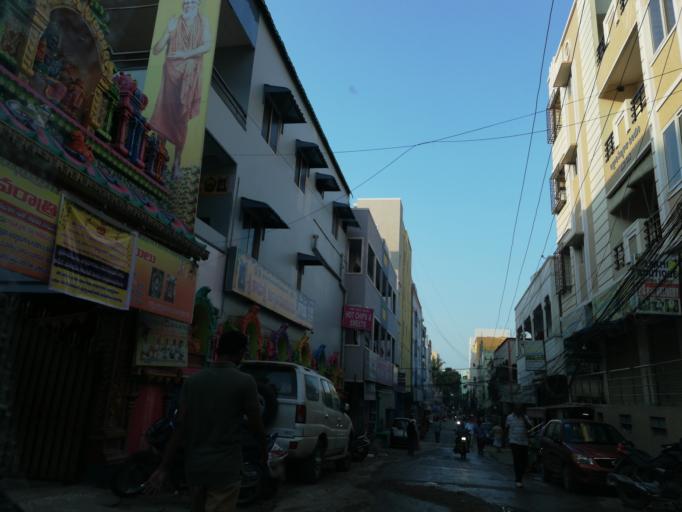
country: IN
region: Telangana
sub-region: Rangareddi
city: Kukatpalli
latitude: 17.4938
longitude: 78.3995
